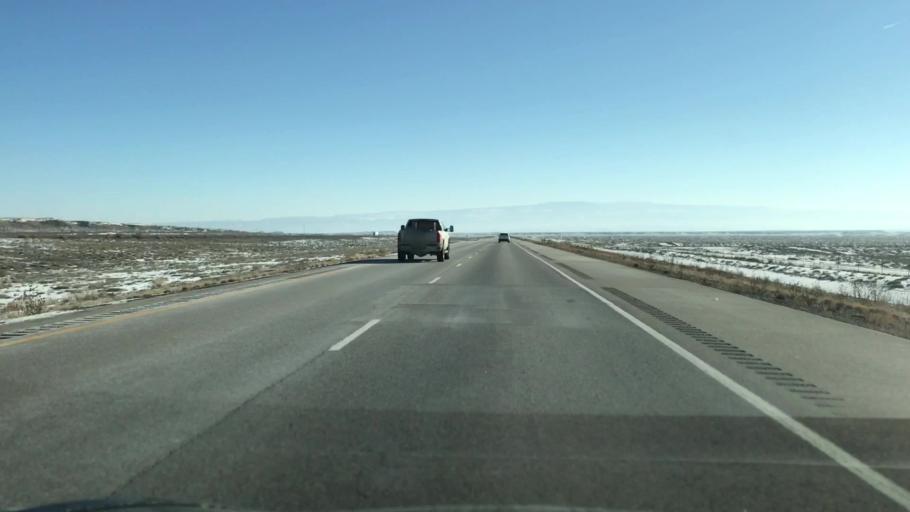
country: US
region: Utah
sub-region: Grand County
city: Moab
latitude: 38.9341
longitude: -109.4547
